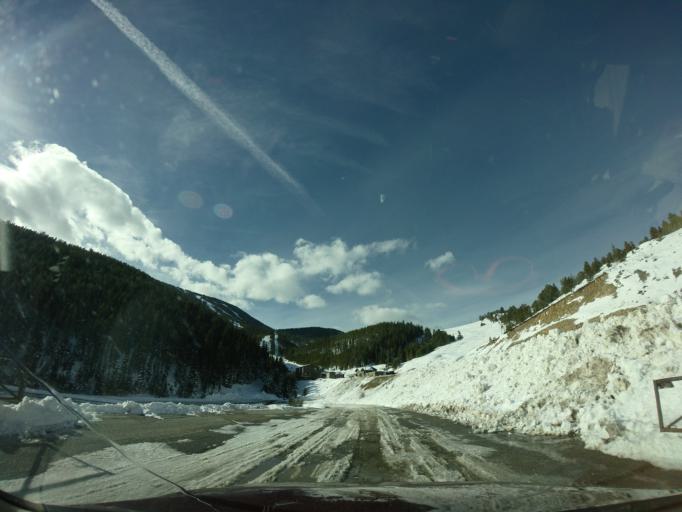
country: US
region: Montana
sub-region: Carbon County
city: Red Lodge
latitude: 45.1908
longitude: -109.3335
